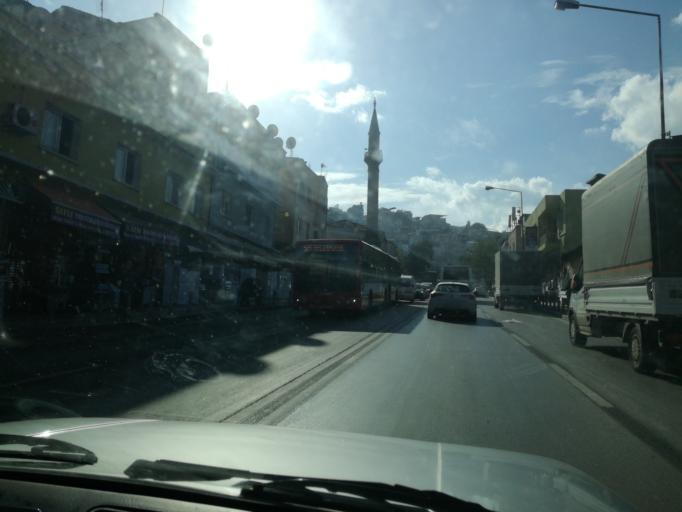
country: TR
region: Izmir
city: Izmir
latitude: 38.4151
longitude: 27.1348
